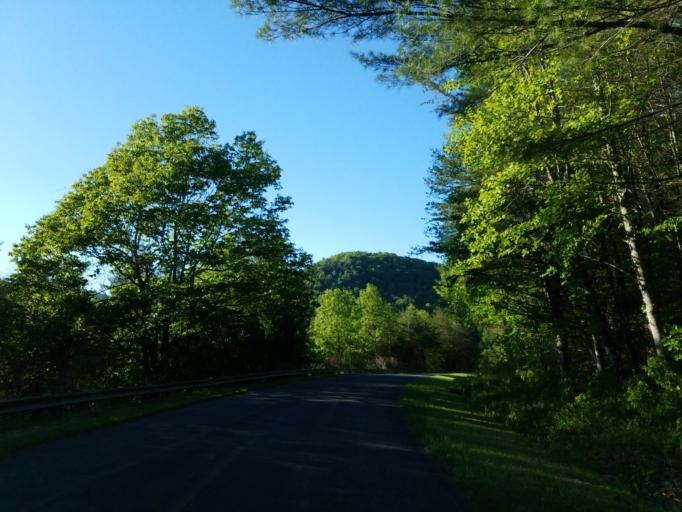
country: US
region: Georgia
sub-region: Fannin County
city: Blue Ridge
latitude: 34.7278
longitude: -84.2846
